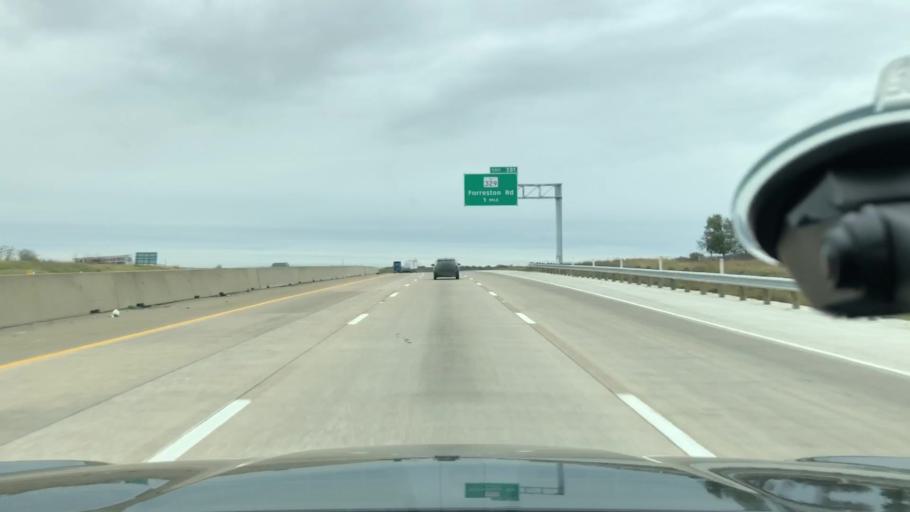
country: US
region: Texas
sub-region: Ellis County
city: Italy
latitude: 32.2405
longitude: -96.8774
